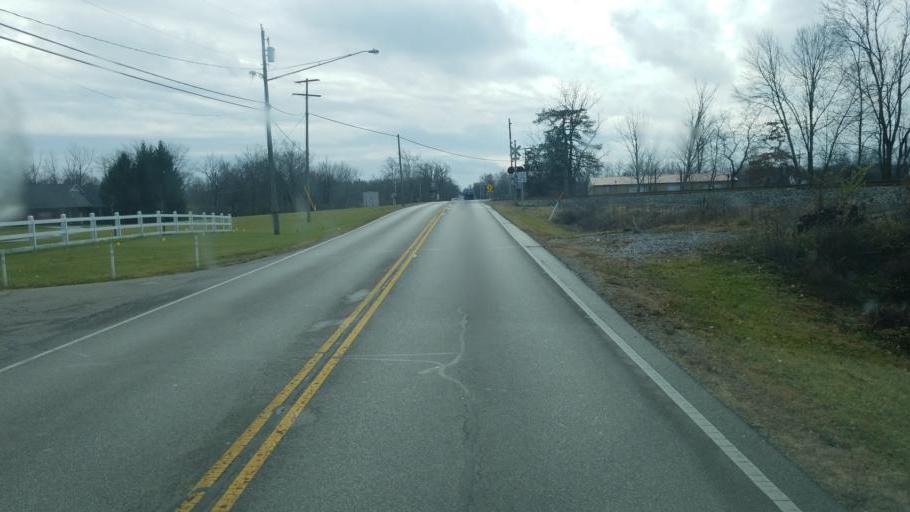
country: US
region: Ohio
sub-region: Delaware County
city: Powell
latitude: 40.1495
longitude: -83.0739
